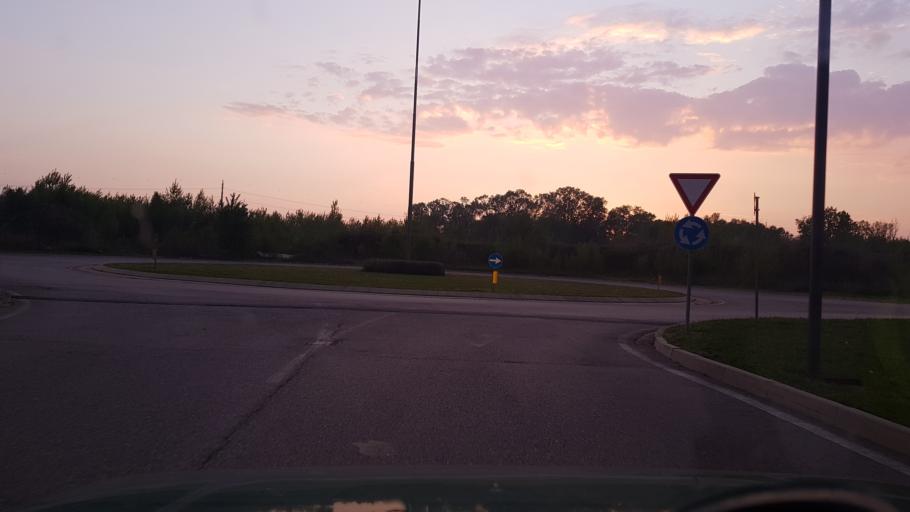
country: IT
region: Friuli Venezia Giulia
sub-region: Provincia di Gorizia
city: Villesse
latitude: 45.8638
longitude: 13.4268
